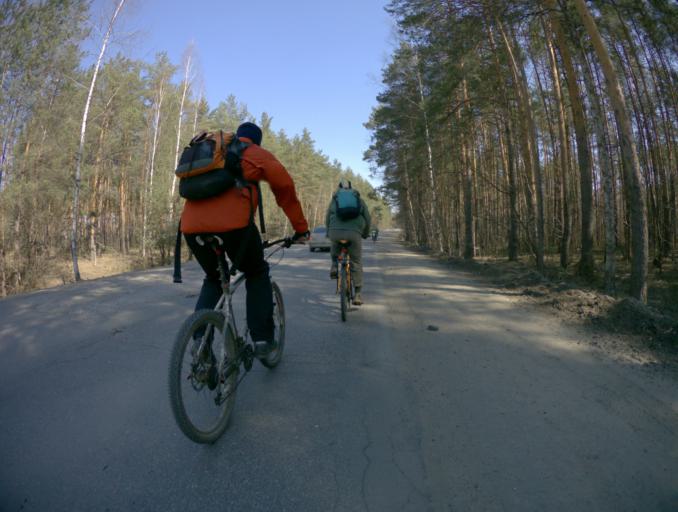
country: RU
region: Vladimir
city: Kommunar
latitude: 56.1295
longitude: 40.4851
